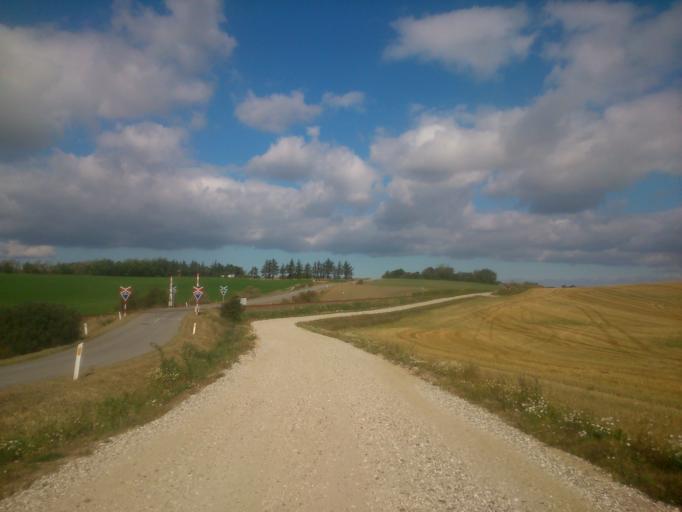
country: DK
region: North Denmark
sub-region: Thisted Kommune
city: Thisted
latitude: 56.9244
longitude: 8.5561
